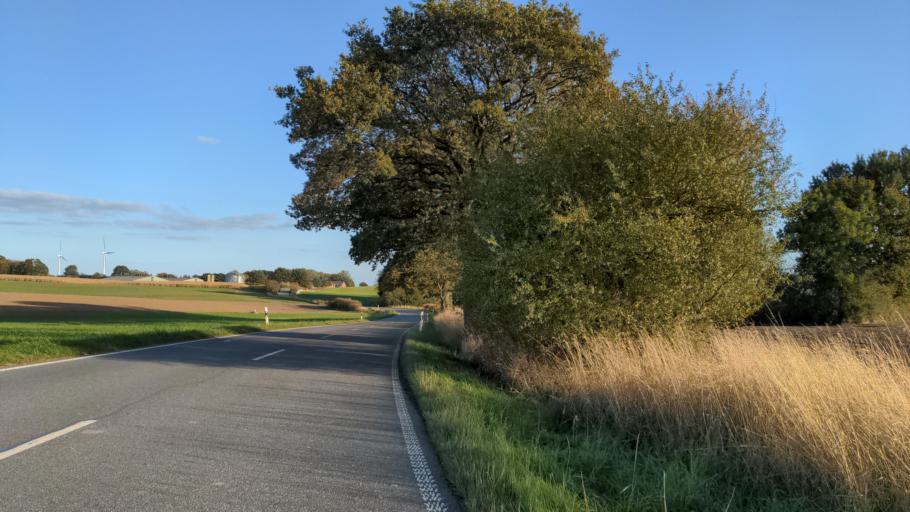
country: DE
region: Schleswig-Holstein
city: Pronstorf
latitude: 53.9623
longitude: 10.5142
